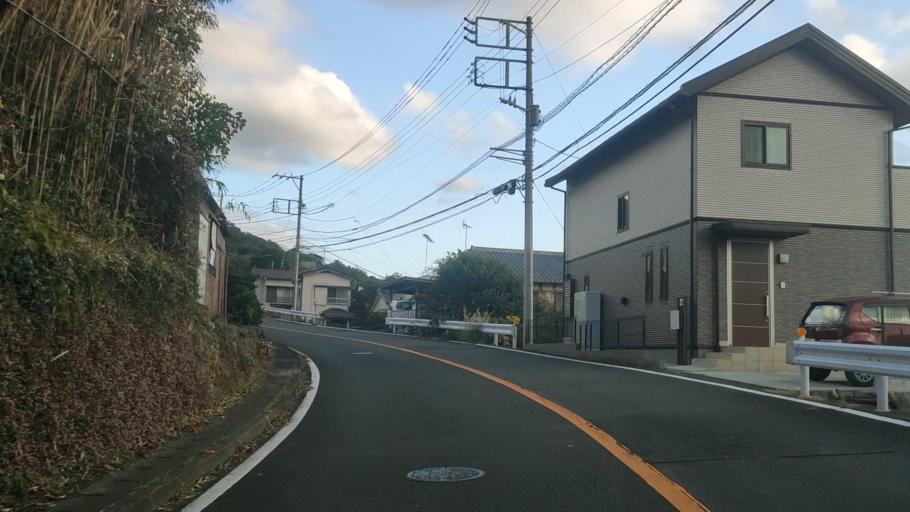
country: JP
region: Shizuoka
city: Ito
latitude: 34.9571
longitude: 139.0810
